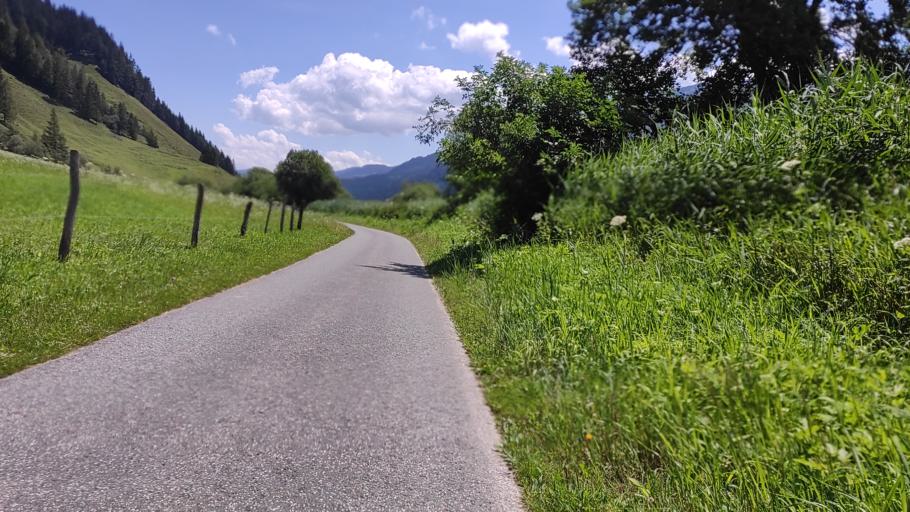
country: AT
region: Tyrol
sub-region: Politischer Bezirk Kitzbuhel
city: Hochfilzen
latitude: 47.4645
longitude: 12.6384
